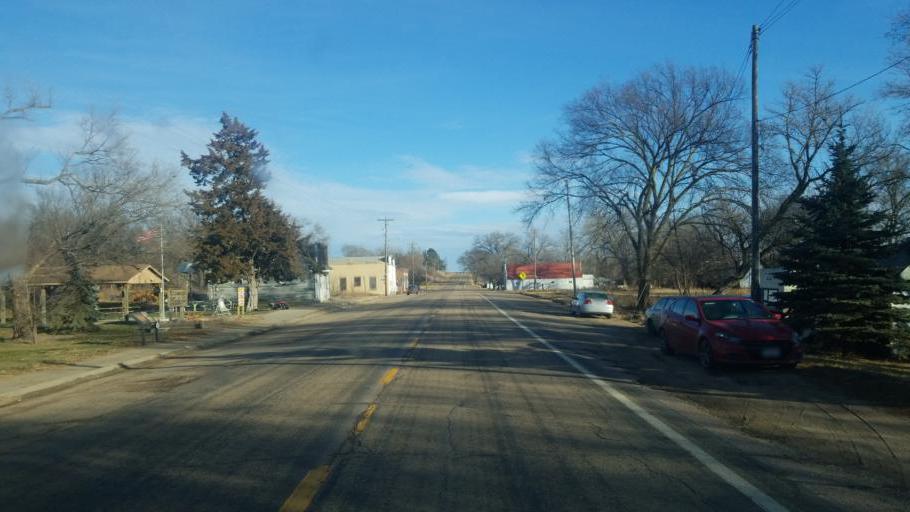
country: US
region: South Dakota
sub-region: Charles Mix County
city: Wagner
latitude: 42.8109
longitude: -98.1939
